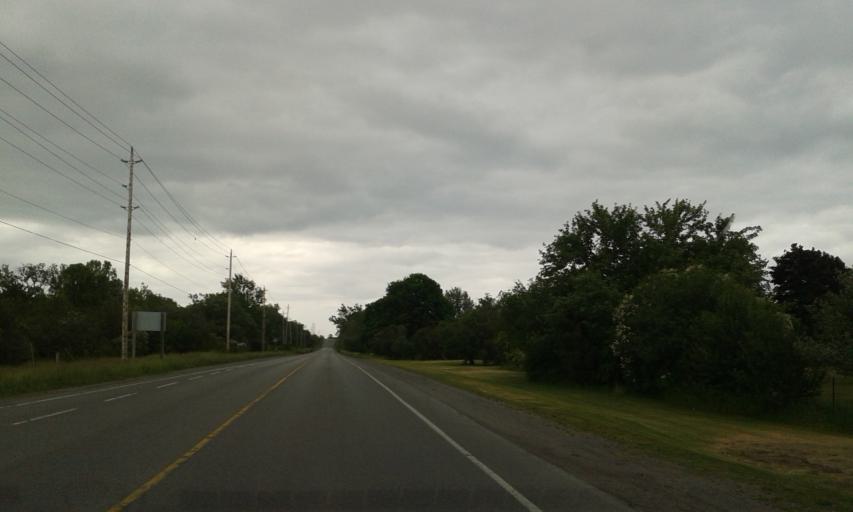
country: CA
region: Ontario
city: Quinte West
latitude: 43.9987
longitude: -77.5189
